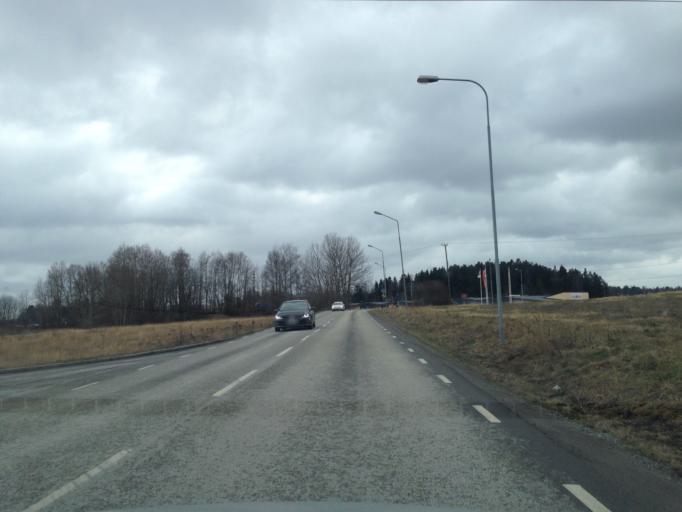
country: SE
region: Stockholm
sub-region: Osterakers Kommun
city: Akersberga
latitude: 59.4906
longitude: 18.2747
